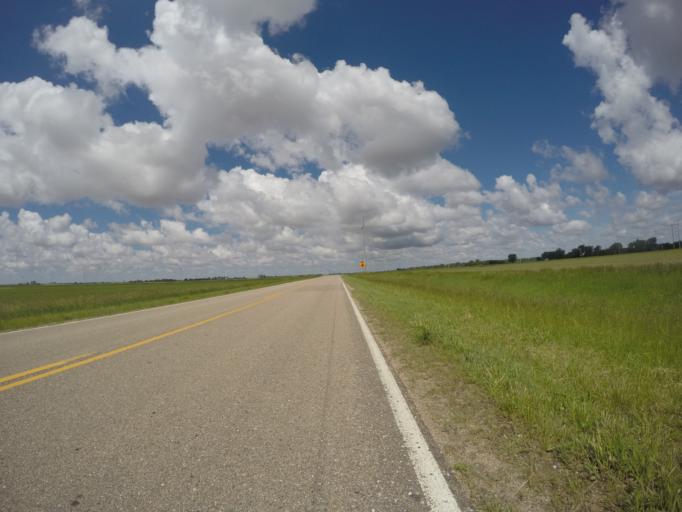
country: US
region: Nebraska
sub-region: Buffalo County
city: Kearney
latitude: 40.6570
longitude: -99.2542
